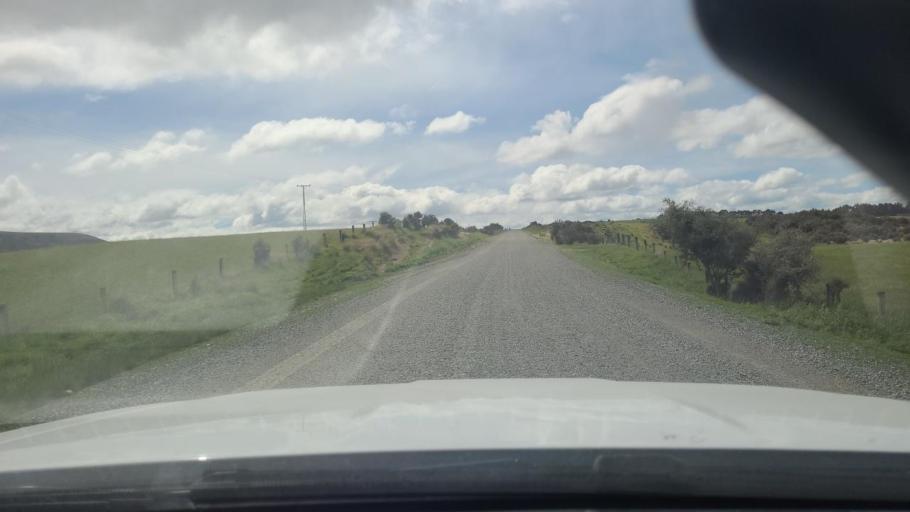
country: NZ
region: Southland
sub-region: Southland District
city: Te Anau
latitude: -45.4812
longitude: 167.9086
